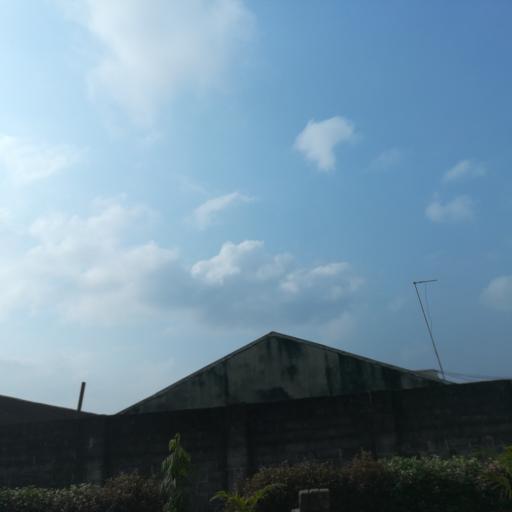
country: NG
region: Rivers
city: Okrika
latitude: 4.7827
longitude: 7.1456
